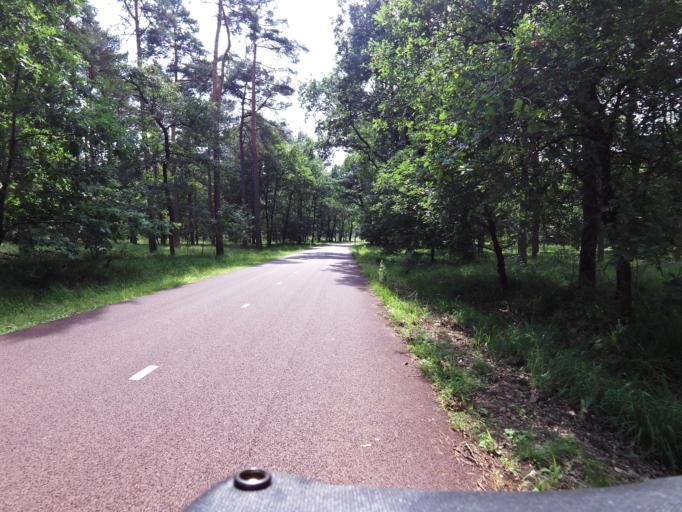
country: NL
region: Limburg
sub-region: Gemeente Roerdalen
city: Vlodrop
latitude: 51.1715
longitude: 6.1361
